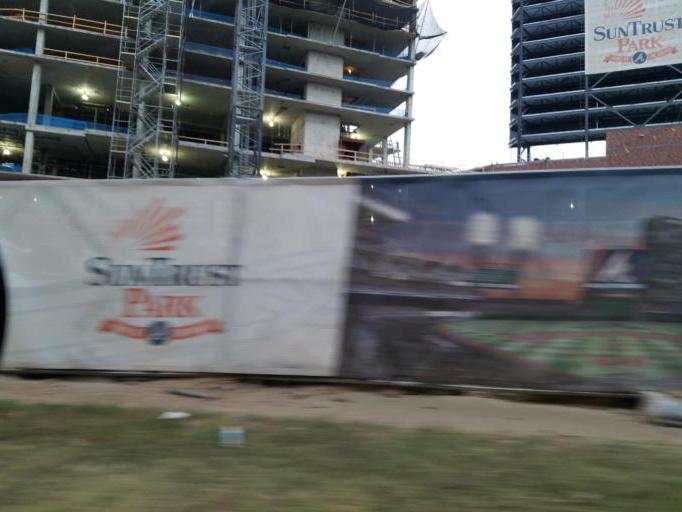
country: US
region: Georgia
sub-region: Cobb County
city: Vinings
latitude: 33.8893
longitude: -84.4670
